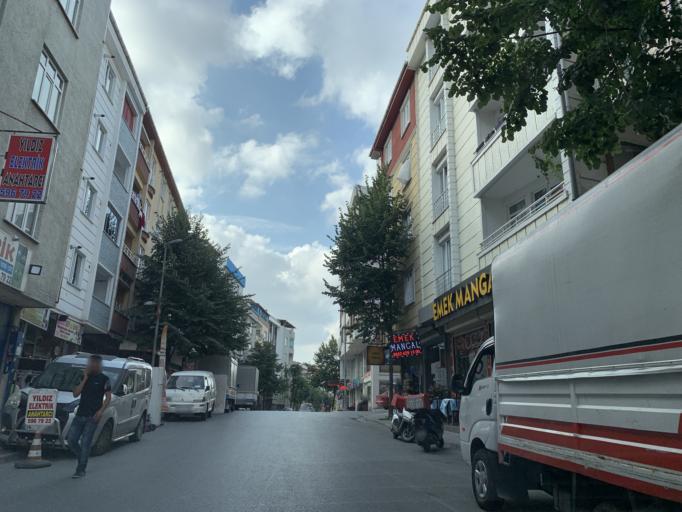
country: TR
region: Istanbul
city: Esenyurt
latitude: 41.0273
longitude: 28.6750
